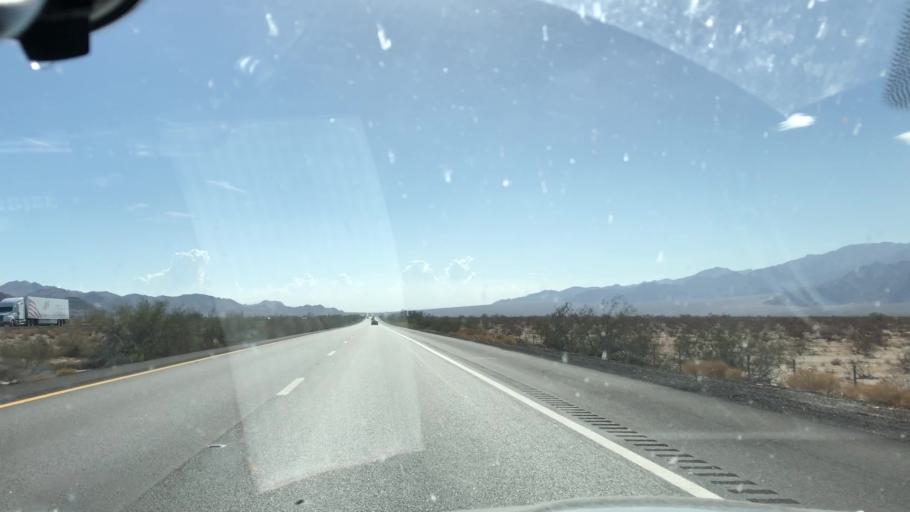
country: US
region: California
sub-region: Imperial County
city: Niland
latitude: 33.6728
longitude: -115.5946
